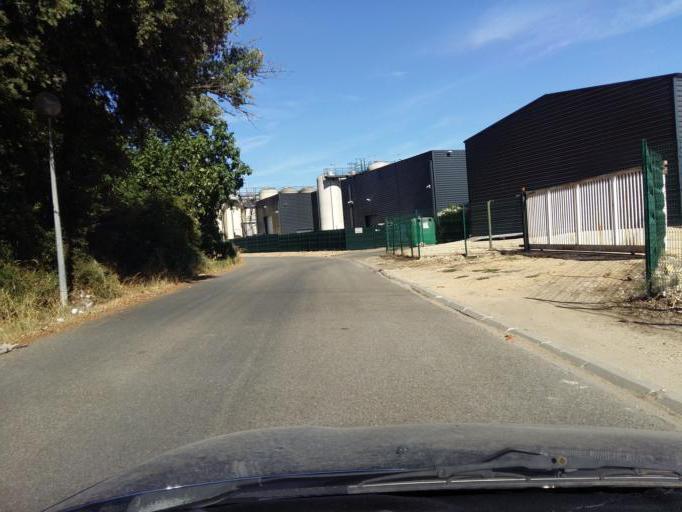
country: FR
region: Provence-Alpes-Cote d'Azur
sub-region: Departement du Vaucluse
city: Piolenc
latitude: 44.1662
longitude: 4.7775
